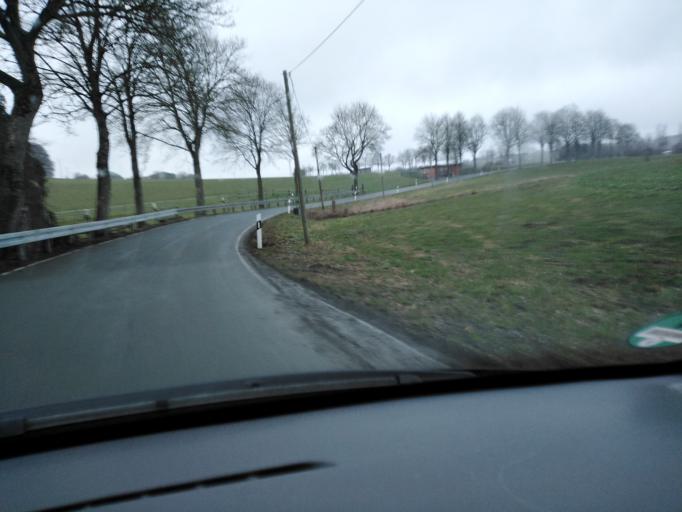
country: DE
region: North Rhine-Westphalia
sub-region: Regierungsbezirk Arnsberg
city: Brilon
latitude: 51.3968
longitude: 8.6320
